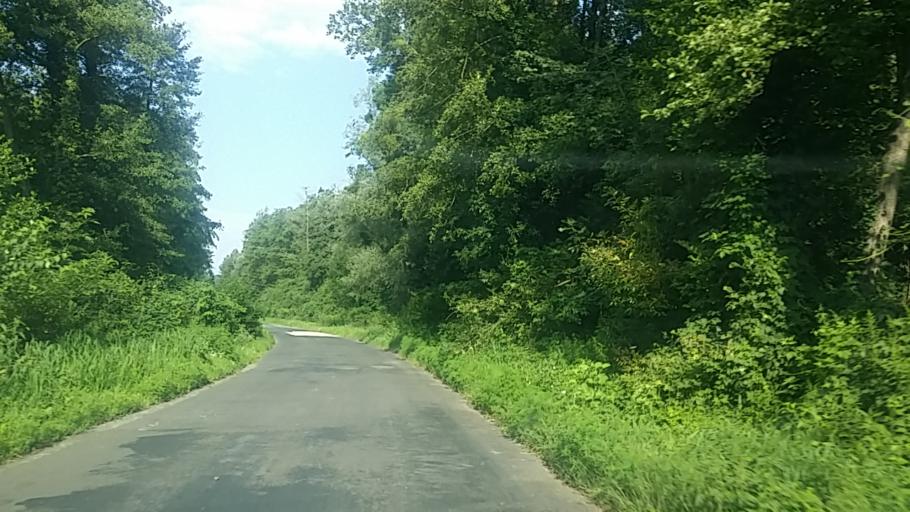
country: HU
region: Zala
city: Lenti
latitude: 46.5557
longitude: 16.5746
